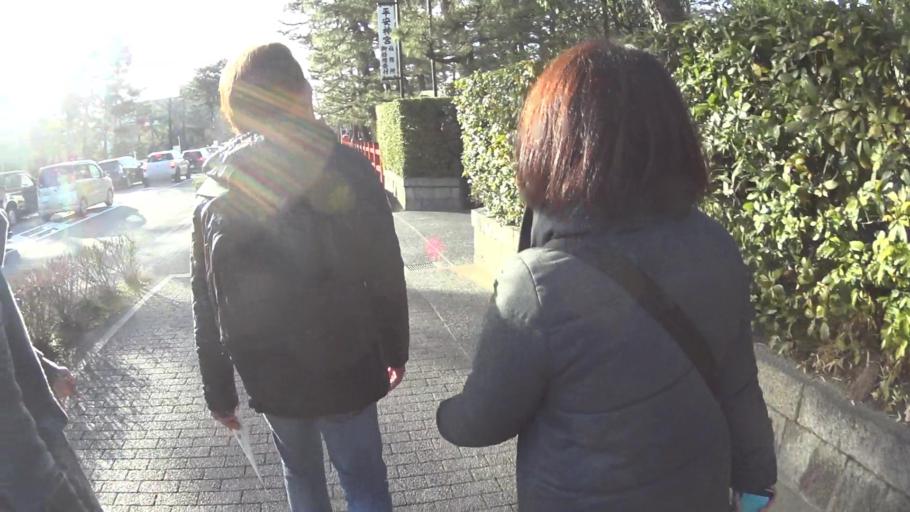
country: JP
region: Kyoto
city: Kyoto
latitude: 35.0153
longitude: 135.7833
